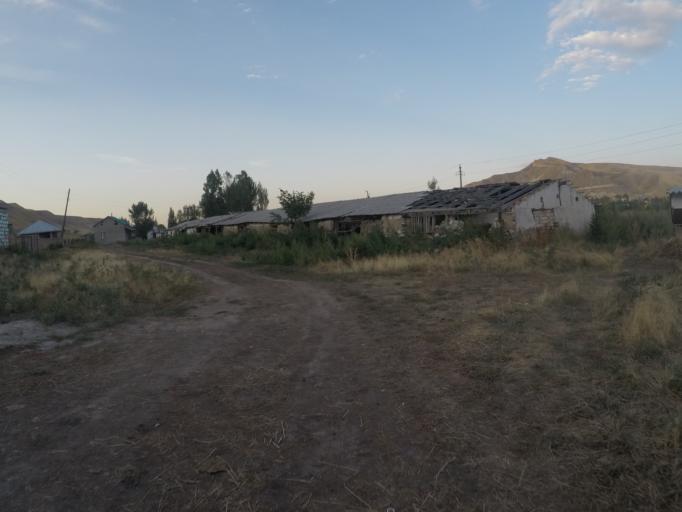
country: KG
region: Chuy
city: Bishkek
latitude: 42.7636
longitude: 74.6379
